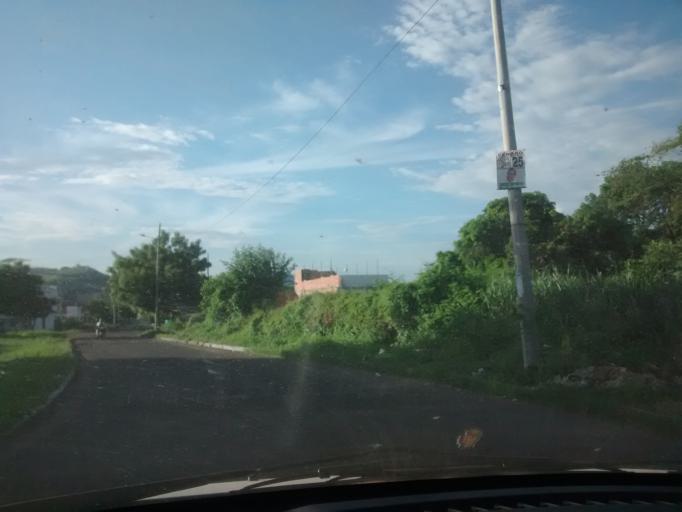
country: CO
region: Cundinamarca
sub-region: Girardot
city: Girardot City
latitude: 4.3058
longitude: -74.8054
